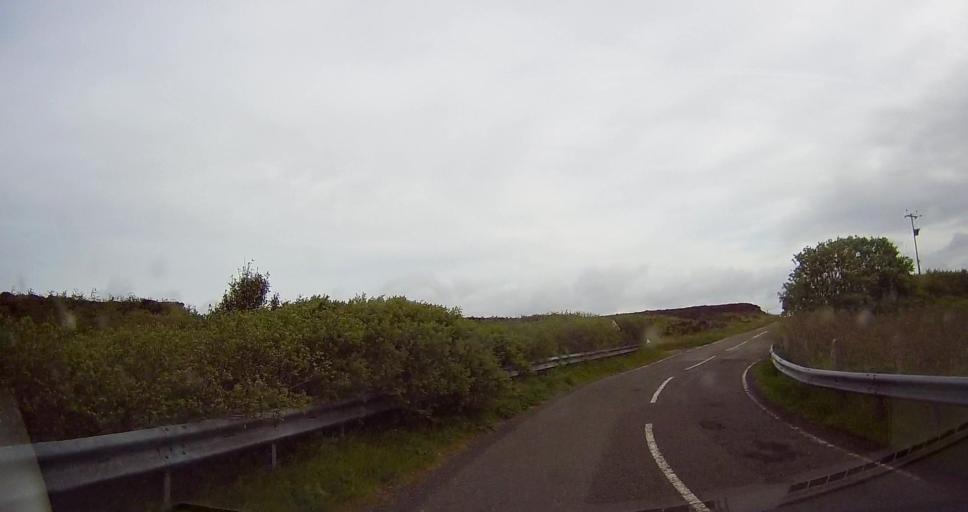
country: GB
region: Scotland
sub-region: Orkney Islands
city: Stromness
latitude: 58.8404
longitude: -3.2164
